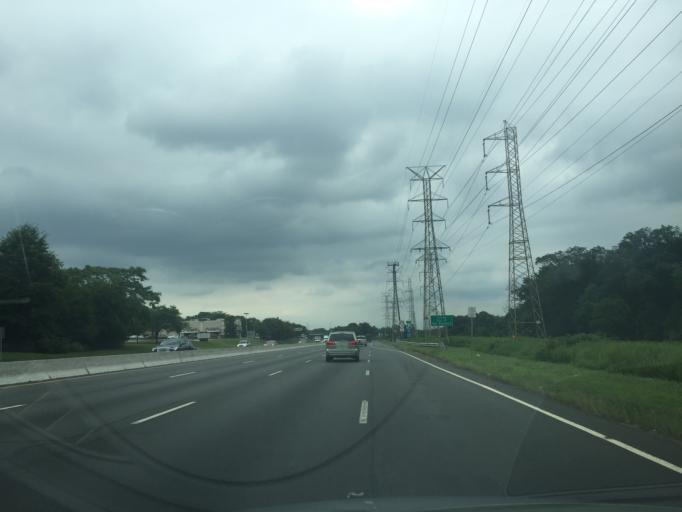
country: US
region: New Jersey
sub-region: Middlesex County
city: Highland Park
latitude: 40.4771
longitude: -74.4243
